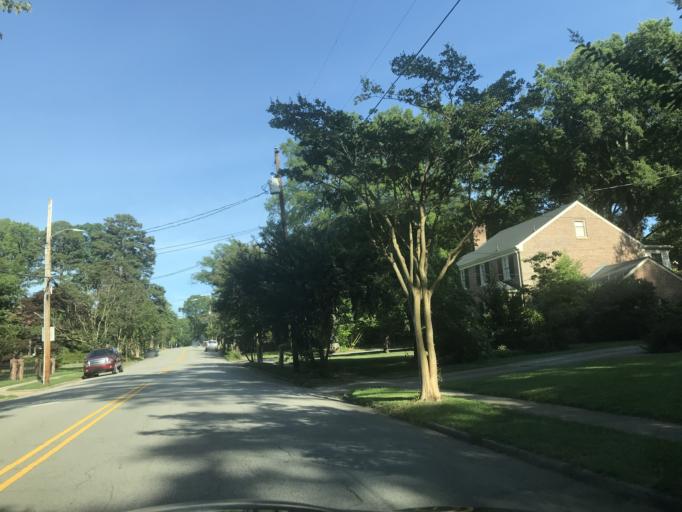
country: US
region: North Carolina
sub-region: Wake County
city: West Raleigh
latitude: 35.7934
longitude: -78.6799
